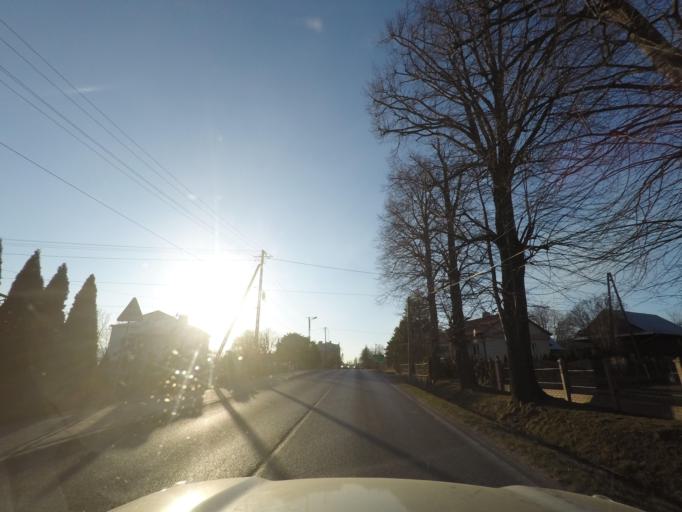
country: PL
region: Subcarpathian Voivodeship
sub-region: Powiat krosnienski
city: Dukla
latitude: 49.5579
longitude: 21.6771
